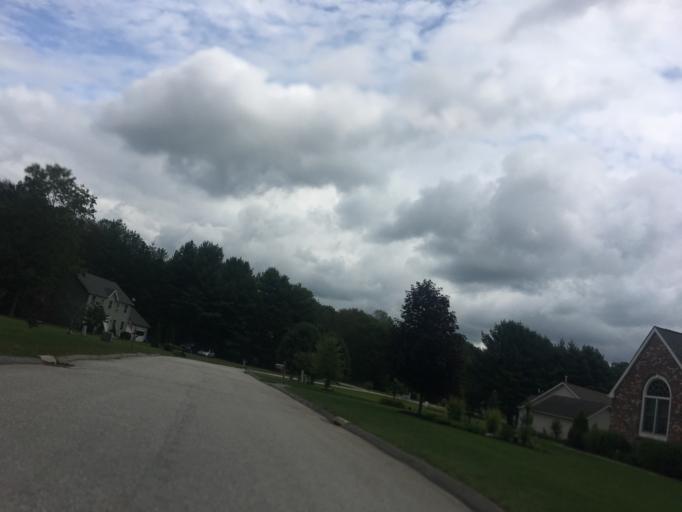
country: US
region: Connecticut
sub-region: Windham County
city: East Brooklyn
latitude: 41.7725
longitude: -71.9040
